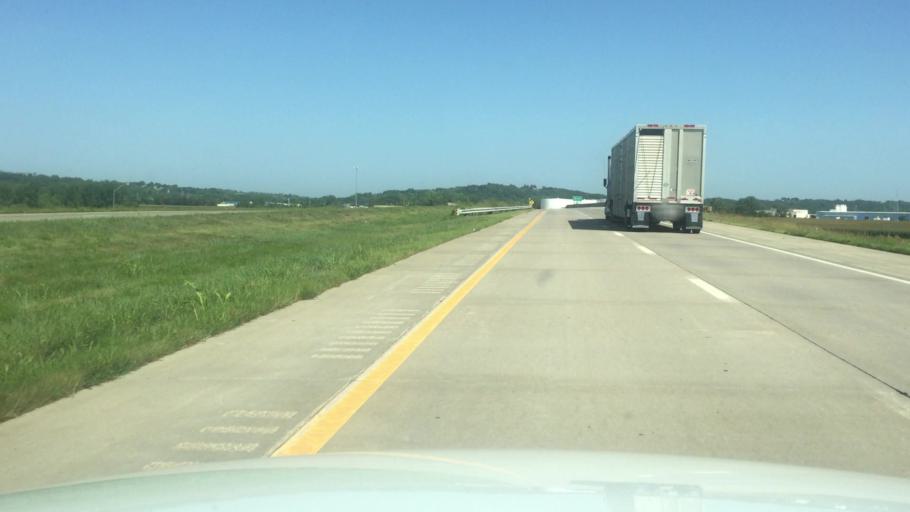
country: US
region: Kansas
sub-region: Doniphan County
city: Wathena
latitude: 39.7458
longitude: -94.9234
